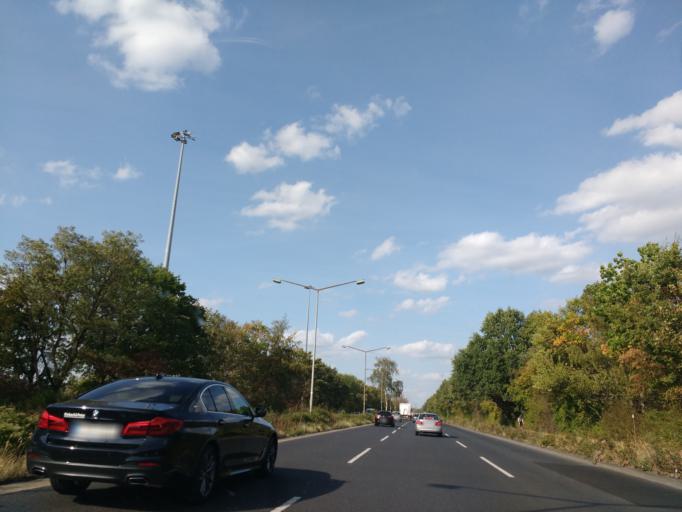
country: DE
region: North Rhine-Westphalia
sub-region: Regierungsbezirk Koln
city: Leverkusen
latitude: 51.0093
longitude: 6.9473
